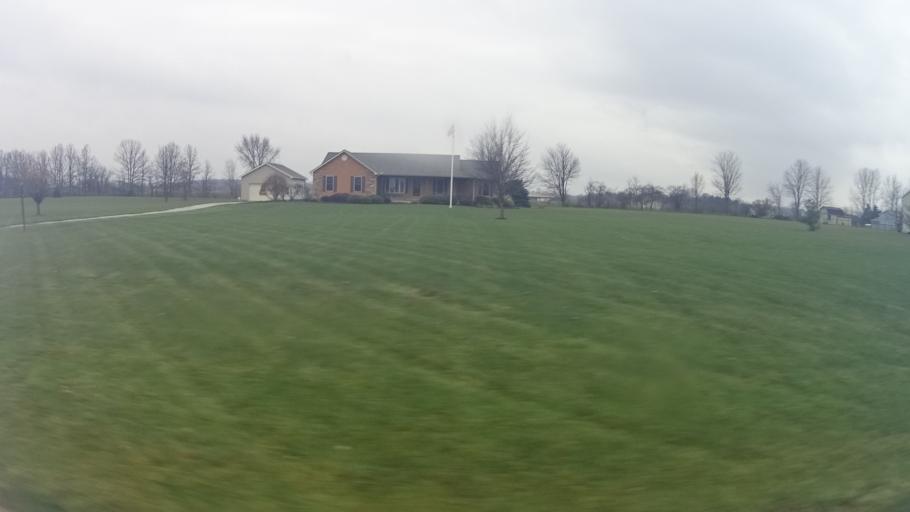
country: US
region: Ohio
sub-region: Lorain County
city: Lagrange
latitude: 41.2609
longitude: -82.1360
